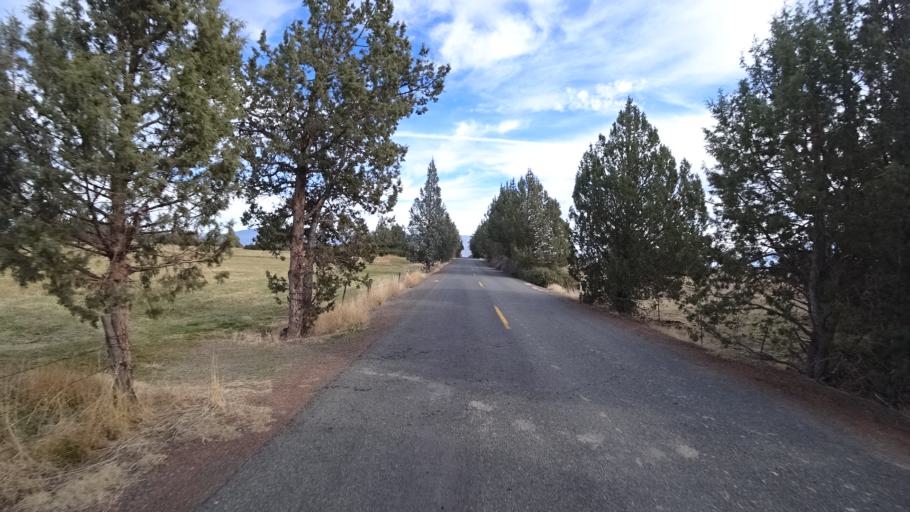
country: US
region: California
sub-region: Siskiyou County
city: Montague
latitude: 41.6385
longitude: -122.4244
